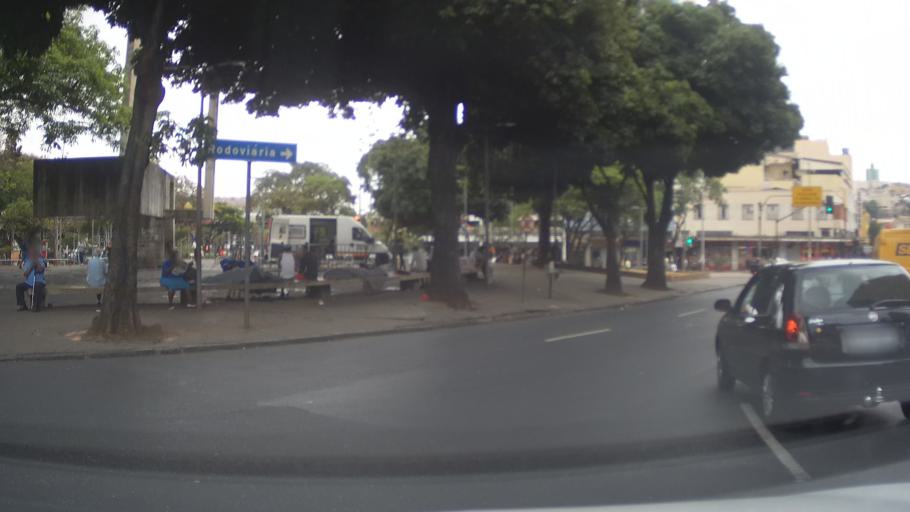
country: BR
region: Minas Gerais
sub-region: Belo Horizonte
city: Belo Horizonte
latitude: -19.9160
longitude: -43.9406
